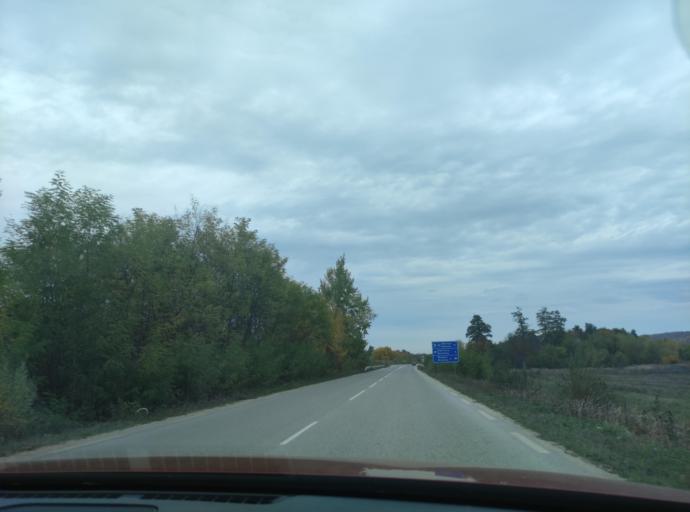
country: BG
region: Montana
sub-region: Obshtina Berkovitsa
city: Berkovitsa
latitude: 43.2415
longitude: 23.1634
